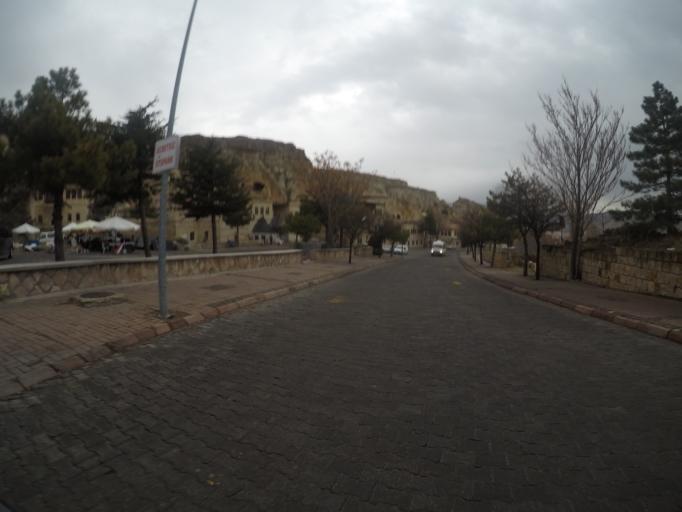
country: TR
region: Nevsehir
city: Urgub
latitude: 38.6332
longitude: 34.9053
